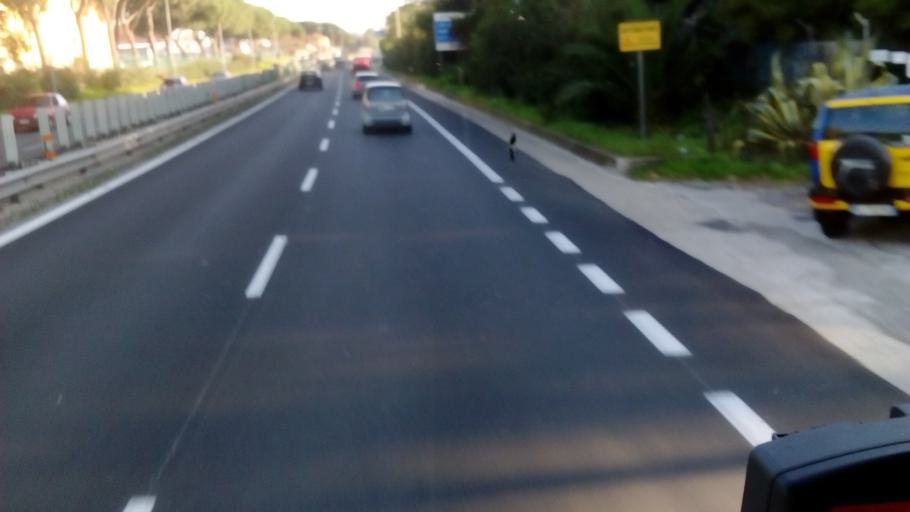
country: IT
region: Latium
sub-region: Citta metropolitana di Roma Capitale
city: Ciampino
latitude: 41.7920
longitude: 12.5926
